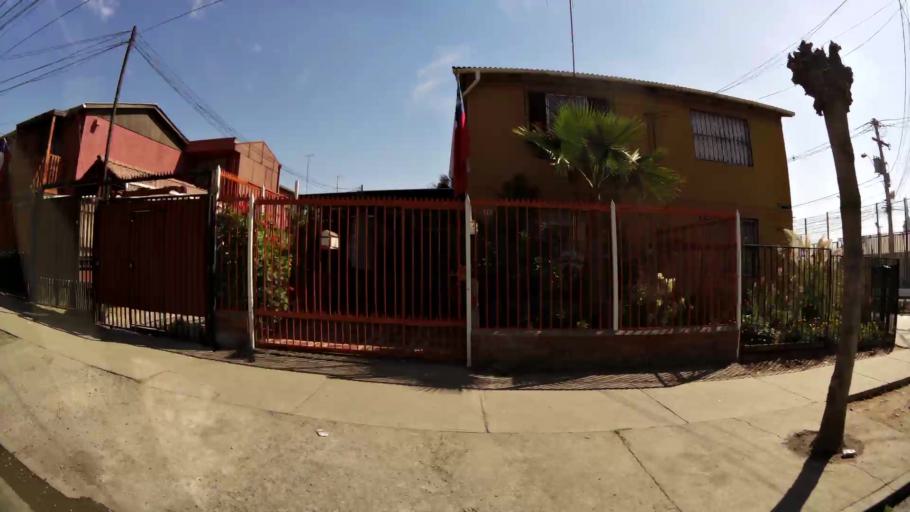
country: CL
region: Santiago Metropolitan
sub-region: Provincia de Cordillera
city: Puente Alto
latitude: -33.6249
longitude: -70.6076
